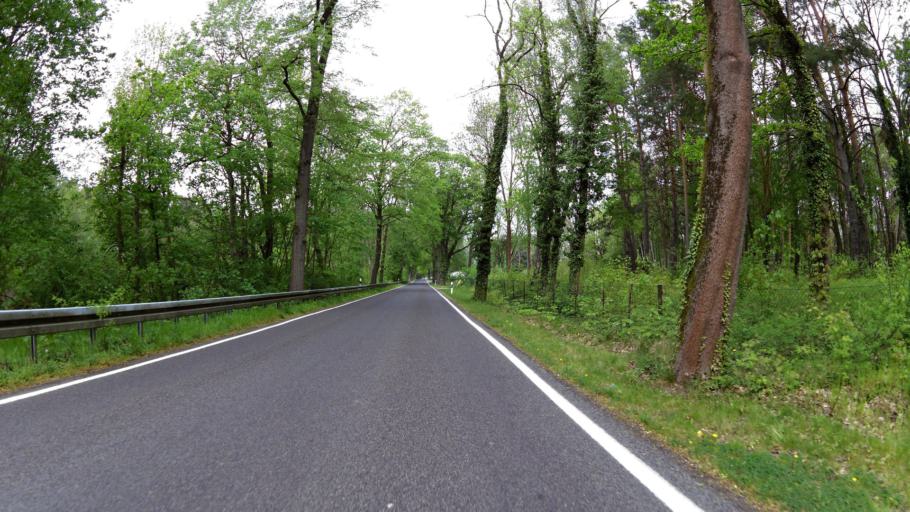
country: DE
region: Brandenburg
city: Mittenwalde
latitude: 52.1978
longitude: 13.5763
